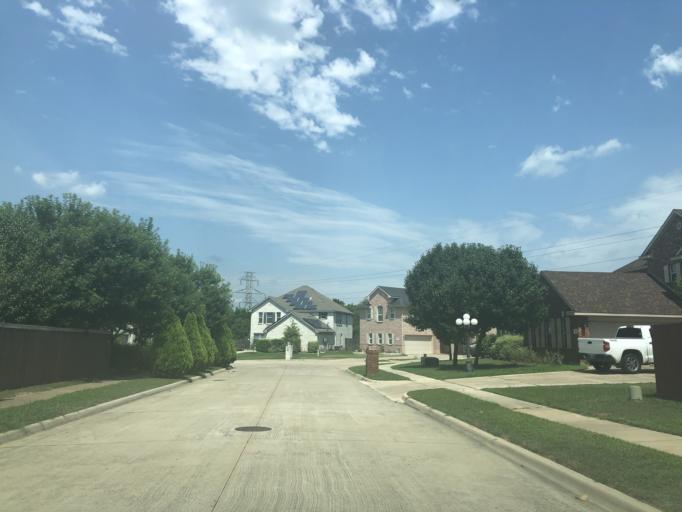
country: US
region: Texas
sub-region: Dallas County
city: Grand Prairie
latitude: 32.7271
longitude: -97.0002
